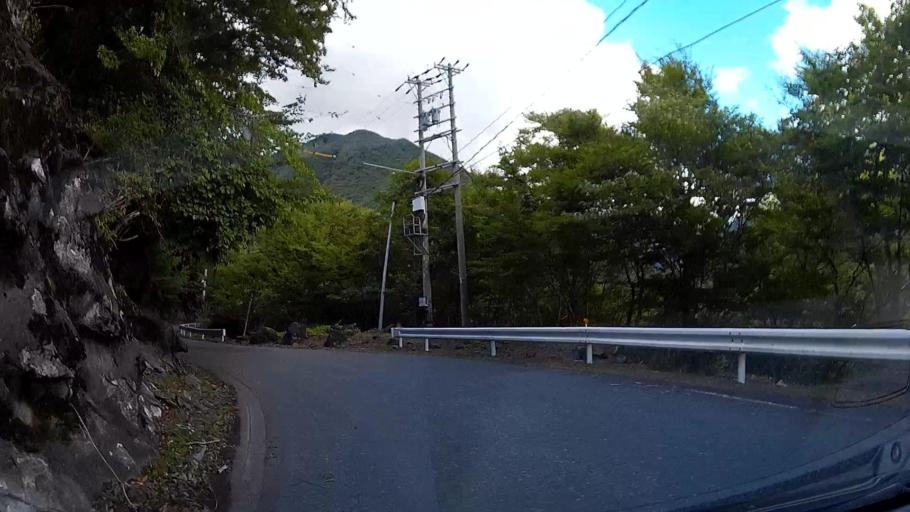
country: JP
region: Shizuoka
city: Shizuoka-shi
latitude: 35.3014
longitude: 138.2169
